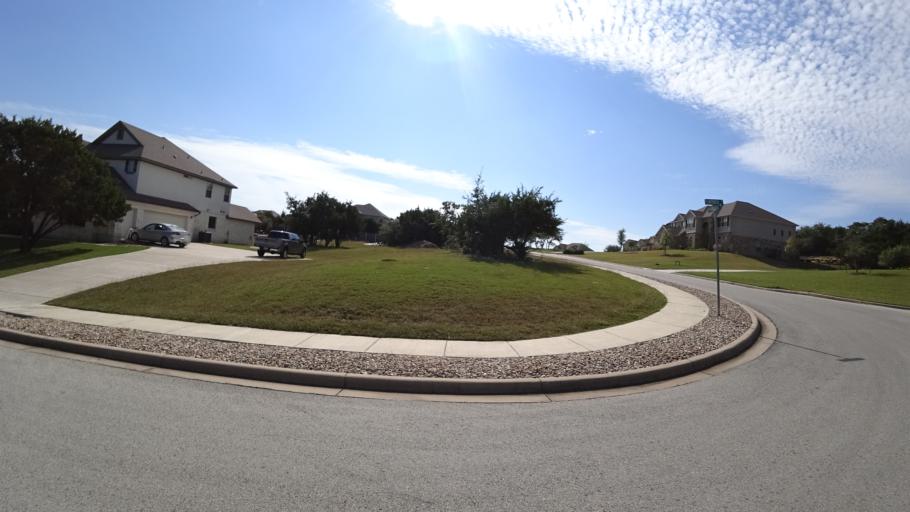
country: US
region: Texas
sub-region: Travis County
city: Bee Cave
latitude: 30.2276
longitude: -97.9323
